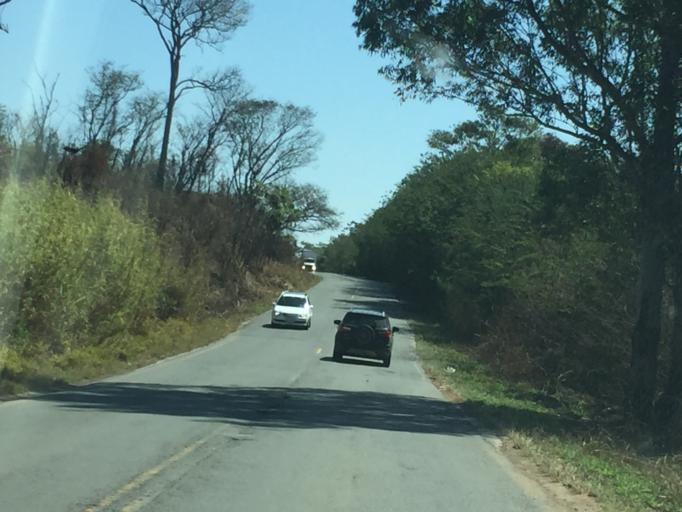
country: BR
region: Sao Paulo
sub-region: Moji-Guacu
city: Mogi-Gaucu
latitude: -22.3558
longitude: -46.8699
